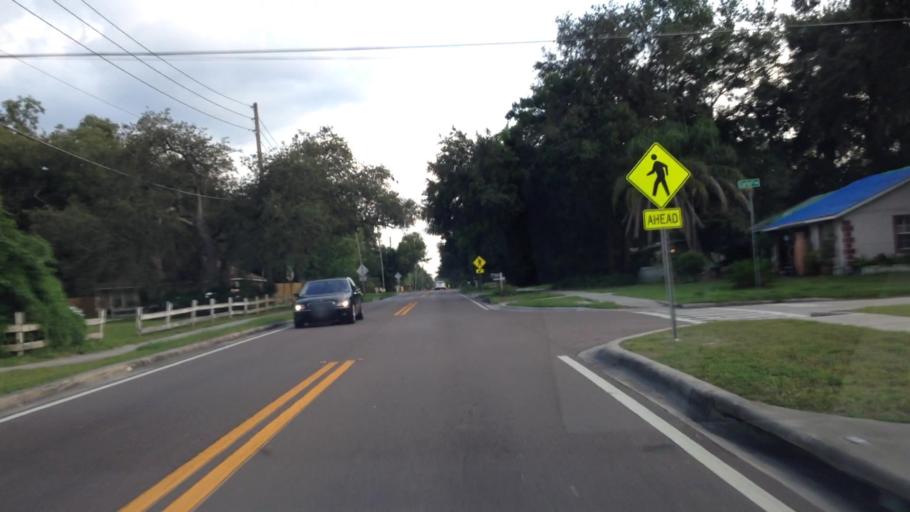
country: US
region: Florida
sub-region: Seminole County
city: Forest City
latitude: 28.6621
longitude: -81.4439
